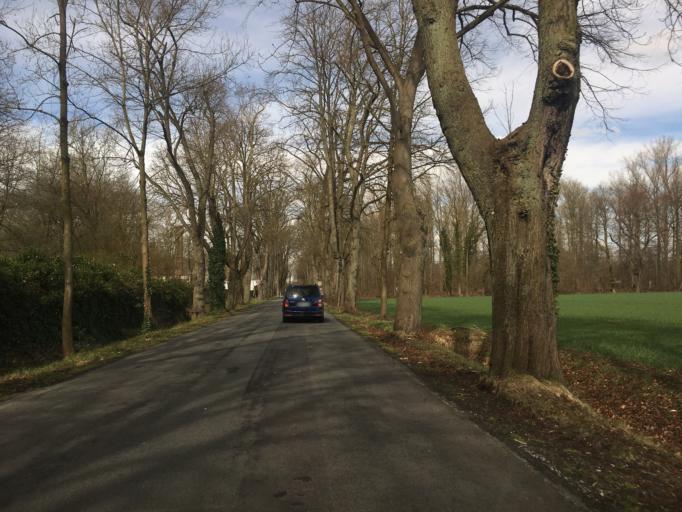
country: DE
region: North Rhine-Westphalia
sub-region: Regierungsbezirk Munster
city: Nordkirchen
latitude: 51.7324
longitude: 7.5401
